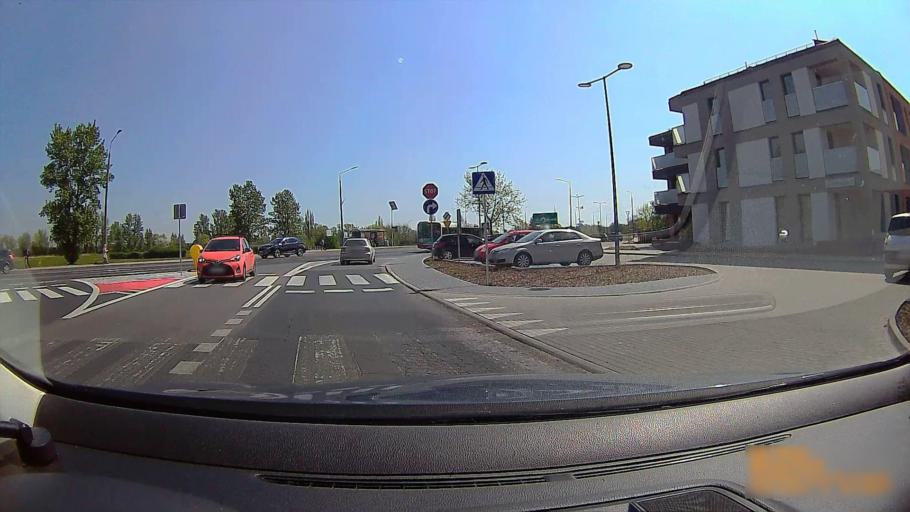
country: PL
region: Greater Poland Voivodeship
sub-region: Konin
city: Konin
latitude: 52.2096
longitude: 18.2587
